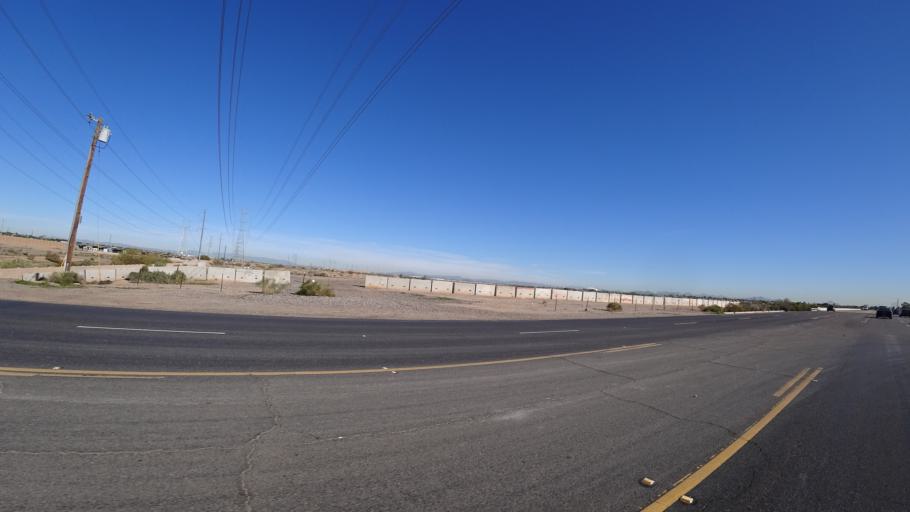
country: US
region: Arizona
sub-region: Maricopa County
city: Litchfield Park
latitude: 33.4931
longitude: -112.3195
